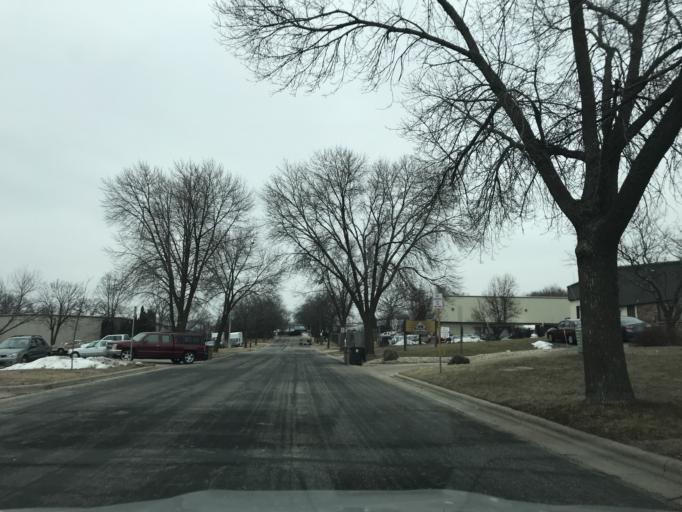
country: US
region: Wisconsin
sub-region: Dane County
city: Monona
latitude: 43.0897
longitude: -89.3079
